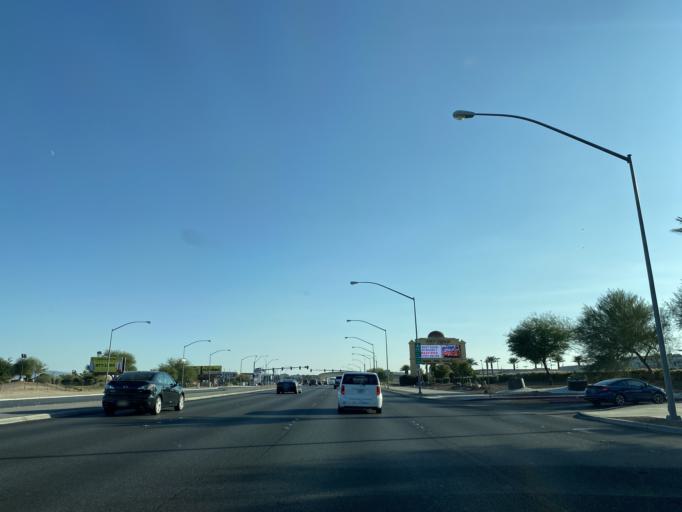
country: US
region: Nevada
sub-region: Clark County
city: Paradise
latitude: 36.0702
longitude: -115.1726
